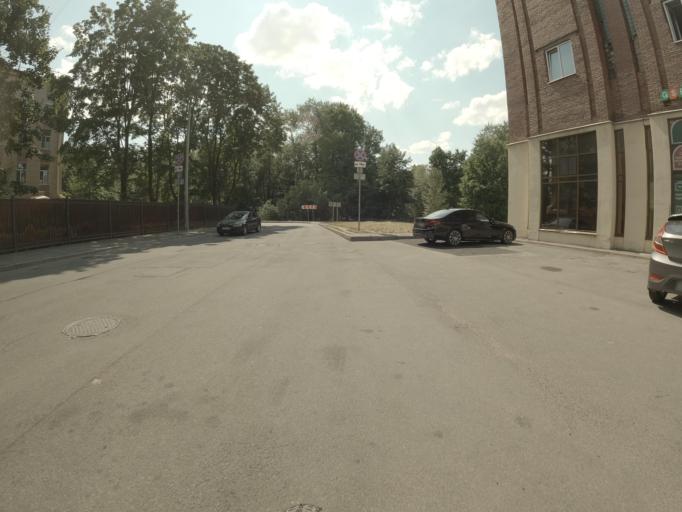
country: RU
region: St.-Petersburg
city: Admiralteisky
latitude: 59.9053
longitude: 30.2668
